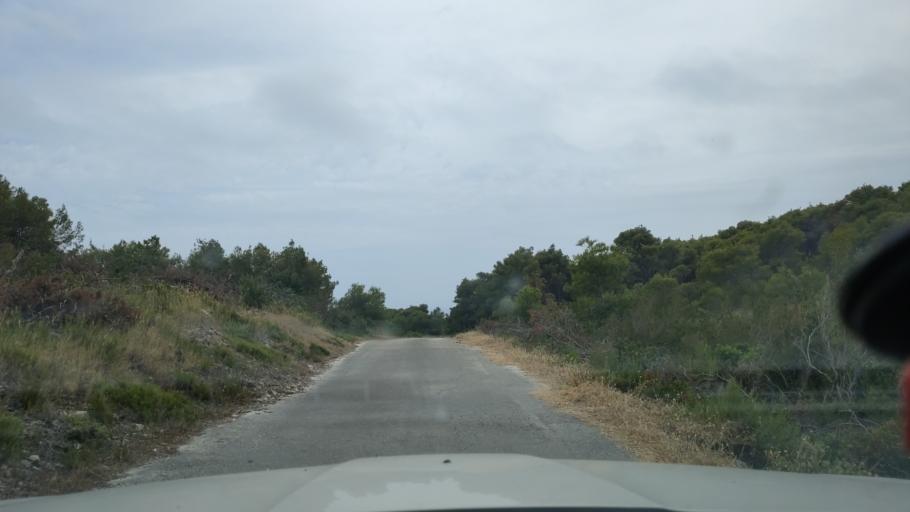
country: HR
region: Splitsko-Dalmatinska
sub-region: Grad Vis
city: Vis
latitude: 43.0281
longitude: 16.1678
